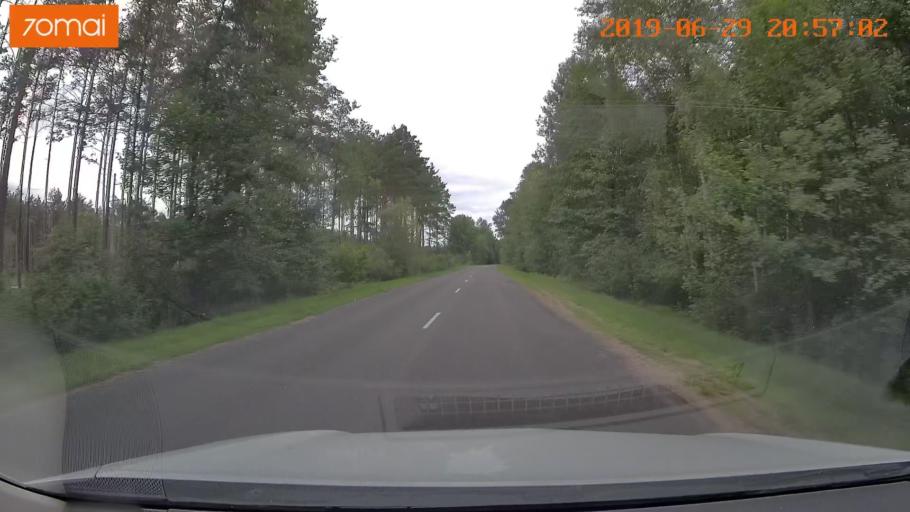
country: BY
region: Brest
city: Hantsavichy
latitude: 52.7134
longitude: 26.3691
